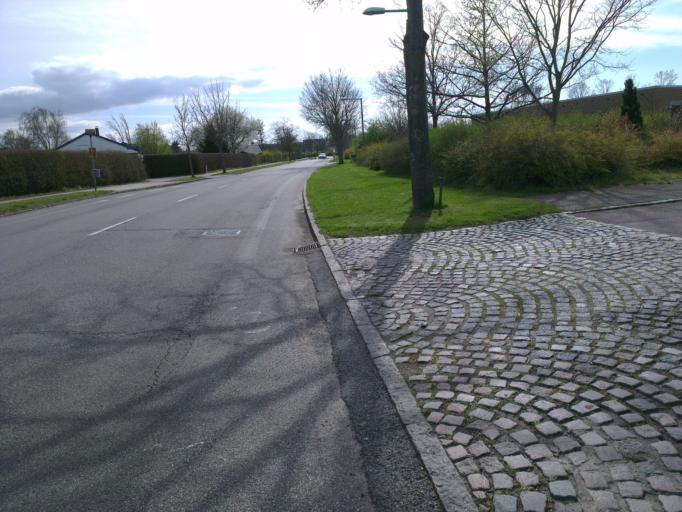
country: DK
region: Capital Region
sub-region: Frederikssund Kommune
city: Frederikssund
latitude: 55.8549
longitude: 12.0591
